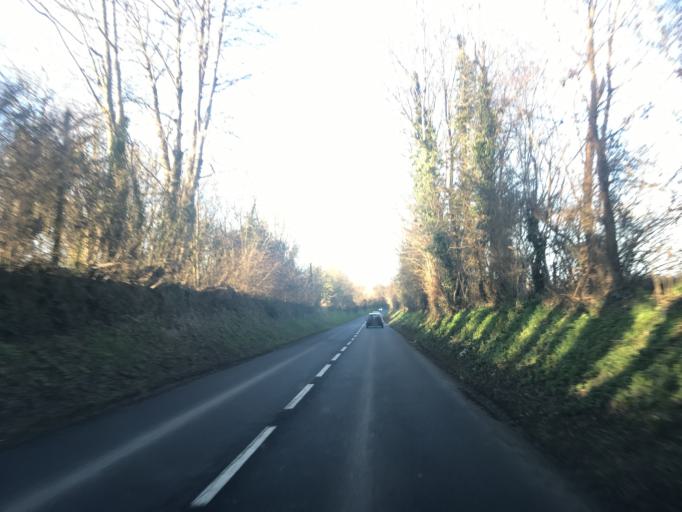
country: FR
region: Lower Normandy
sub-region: Departement du Calvados
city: Beuville
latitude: 49.2179
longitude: -0.3391
